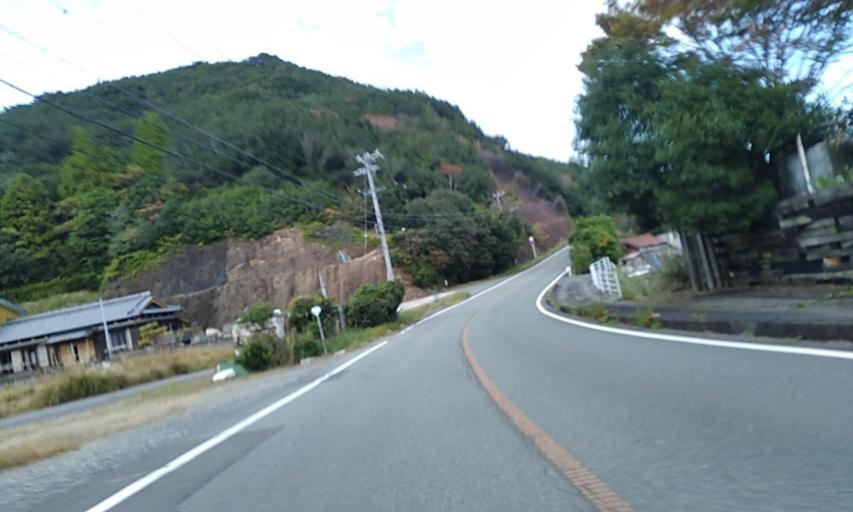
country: JP
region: Mie
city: Ise
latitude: 34.3136
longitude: 136.6425
